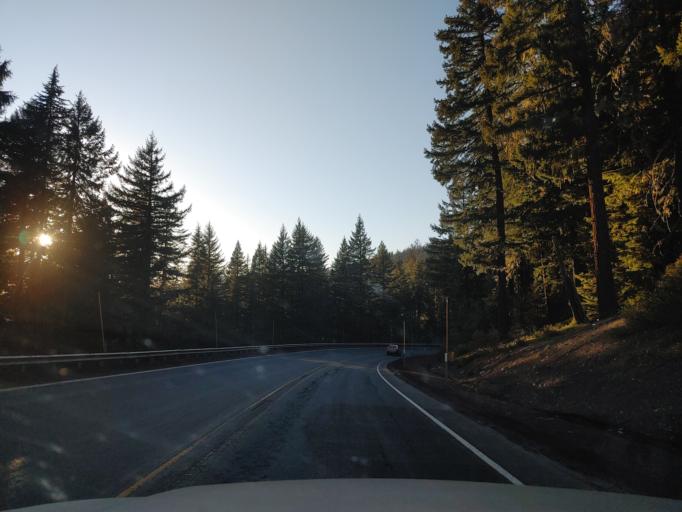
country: US
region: Oregon
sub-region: Lane County
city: Oakridge
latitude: 43.6138
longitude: -122.0685
